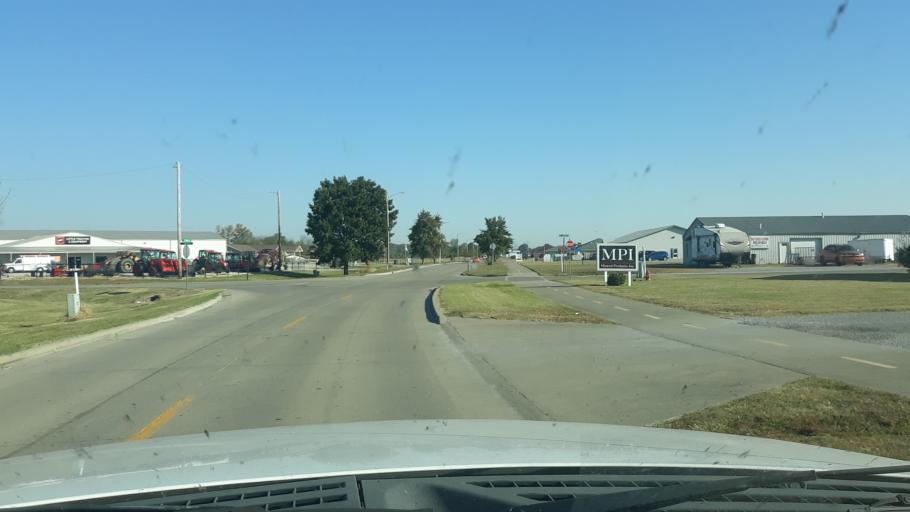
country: US
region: Illinois
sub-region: Saline County
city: Harrisburg
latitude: 37.7436
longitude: -88.5316
